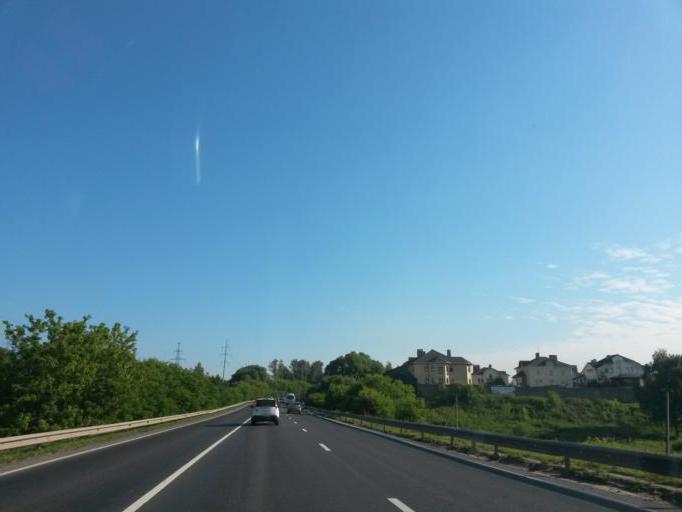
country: RU
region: Moskovskaya
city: Yam
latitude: 55.5000
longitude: 37.7503
